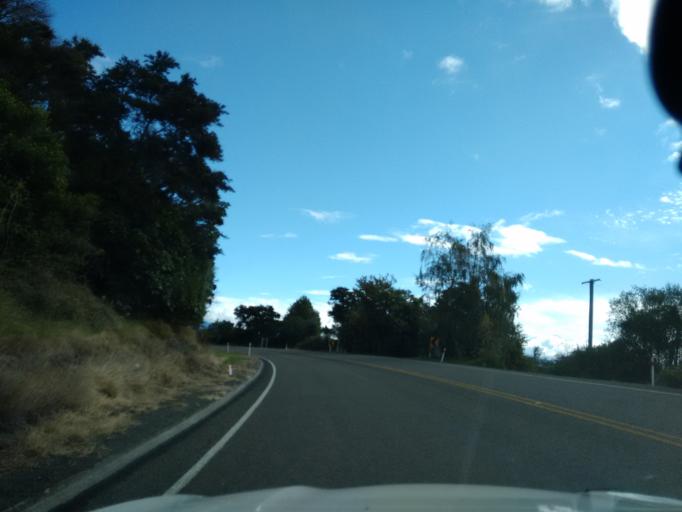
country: NZ
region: Waikato
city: Turangi
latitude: -38.8869
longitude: 175.9543
